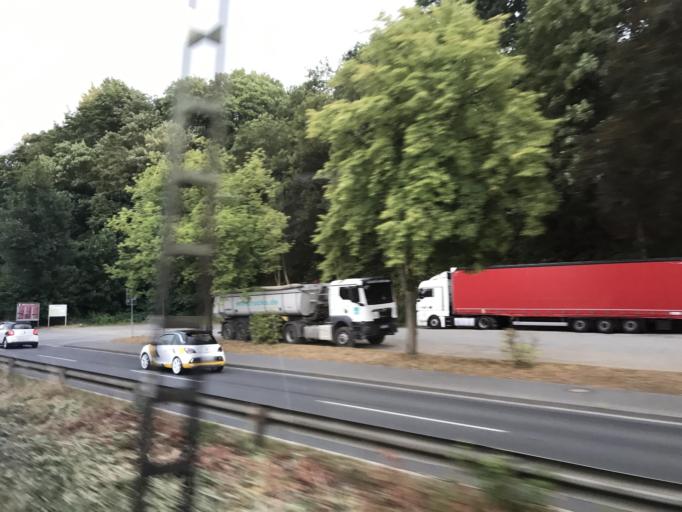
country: DE
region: North Rhine-Westphalia
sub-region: Regierungsbezirk Koln
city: Eitorf
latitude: 50.7753
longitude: 7.4394
